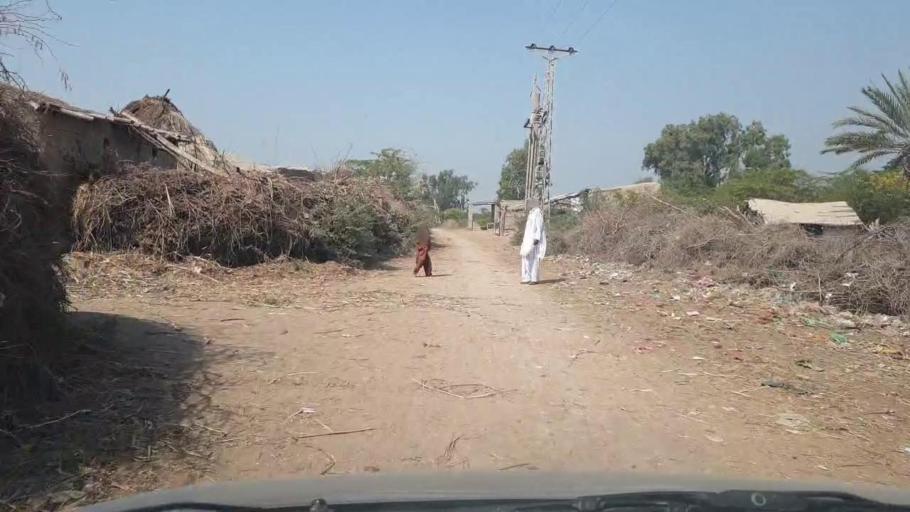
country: PK
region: Sindh
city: Mirwah Gorchani
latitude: 25.3565
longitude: 69.1457
